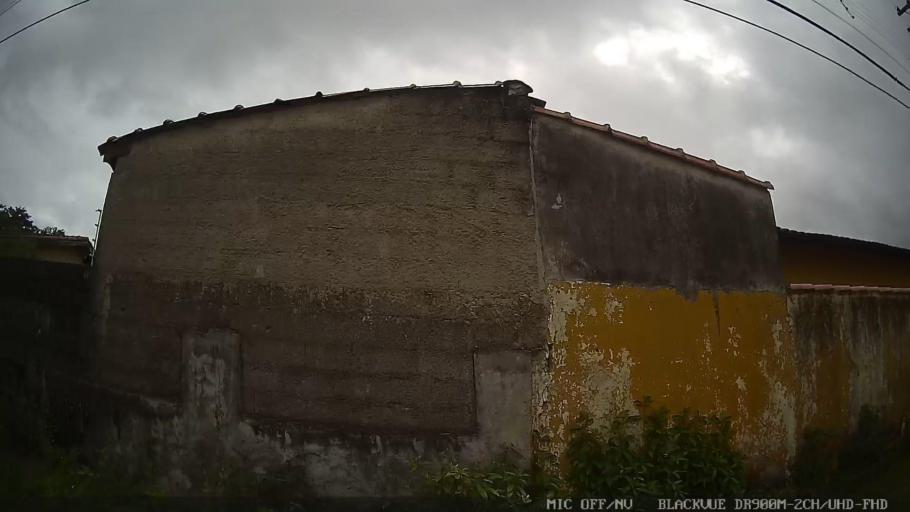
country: BR
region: Sao Paulo
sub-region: Itanhaem
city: Itanhaem
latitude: -24.1571
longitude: -46.7426
